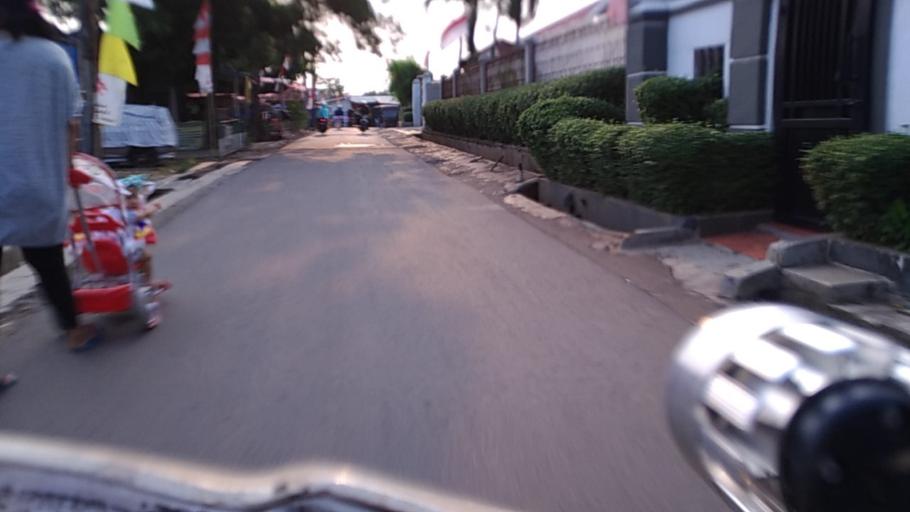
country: ID
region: West Java
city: Depok
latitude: -6.3652
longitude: 106.8847
